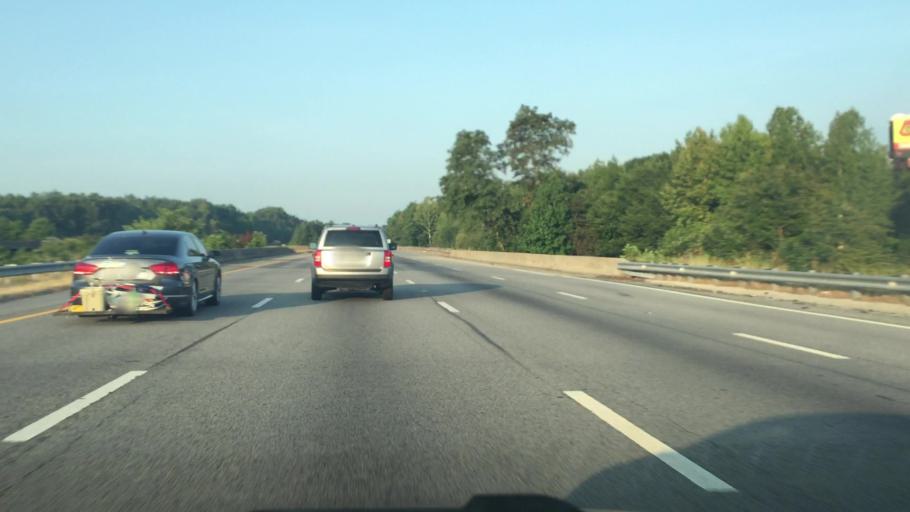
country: US
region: North Carolina
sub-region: Randolph County
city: Trinity
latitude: 35.8768
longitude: -80.0049
